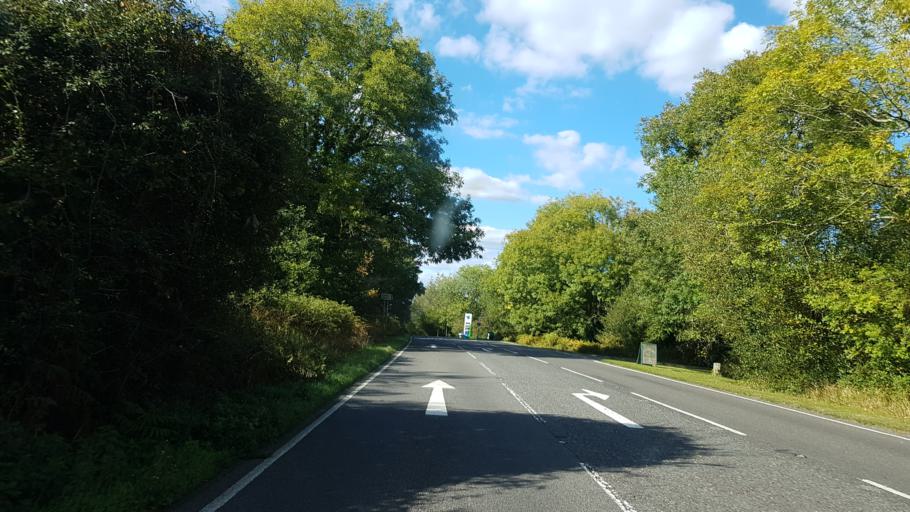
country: GB
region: England
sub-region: West Sussex
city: Petworth
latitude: 51.0258
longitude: -0.6256
